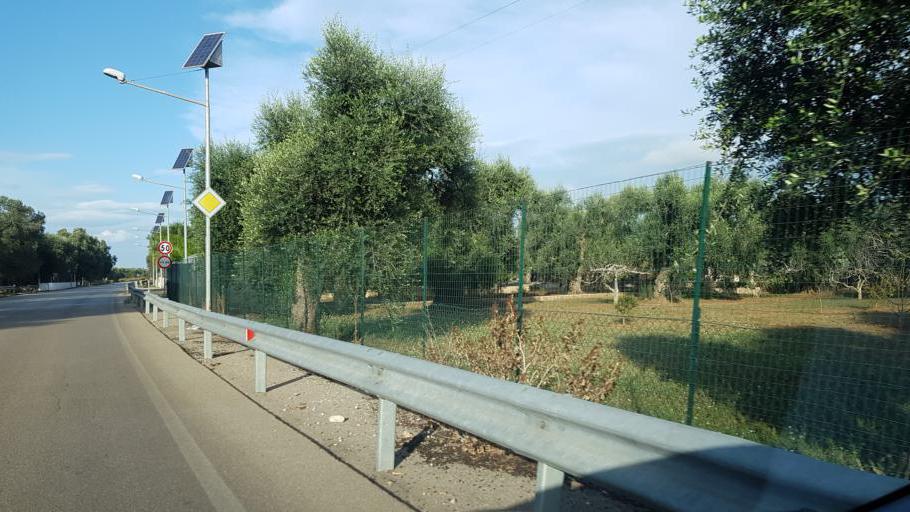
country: IT
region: Apulia
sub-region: Provincia di Brindisi
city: Oria
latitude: 40.5270
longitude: 17.6540
